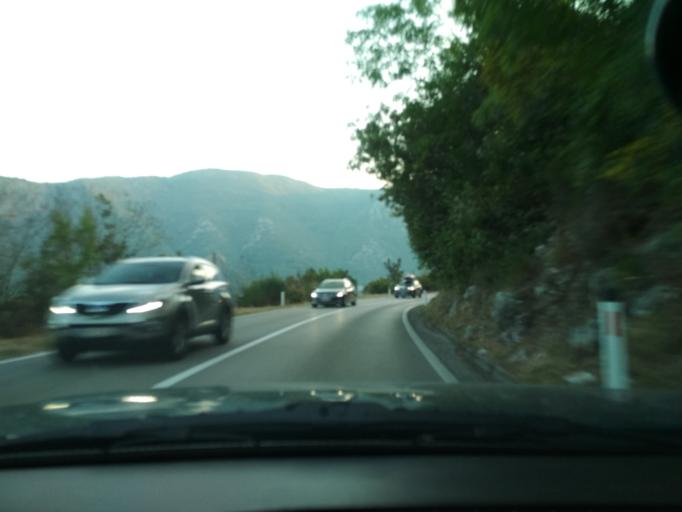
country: ME
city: Lipci
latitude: 42.5038
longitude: 18.6673
